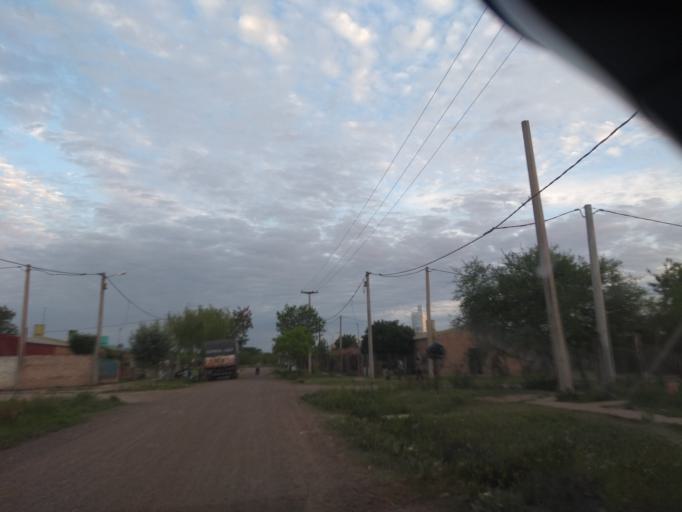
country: AR
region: Chaco
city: Fontana
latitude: -27.4153
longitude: -59.0539
